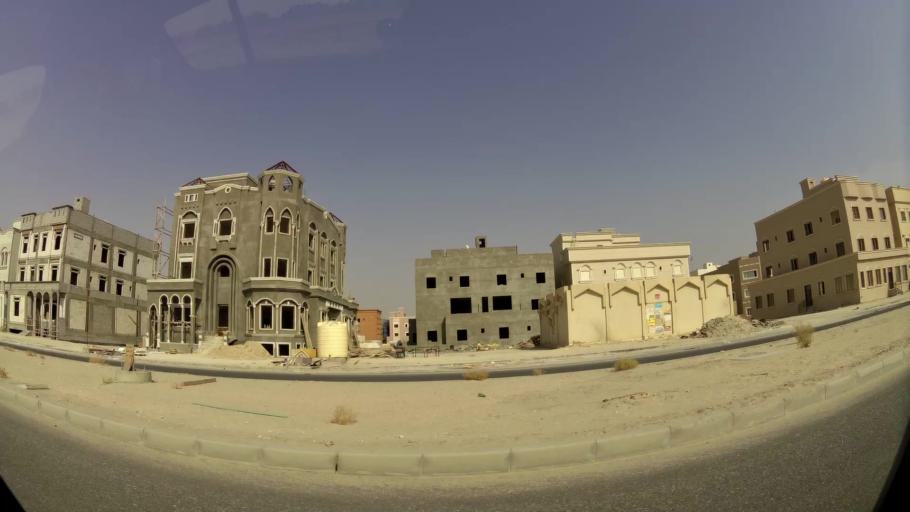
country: KW
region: Muhafazat al Jahra'
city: Al Jahra'
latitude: 29.3451
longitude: 47.7706
